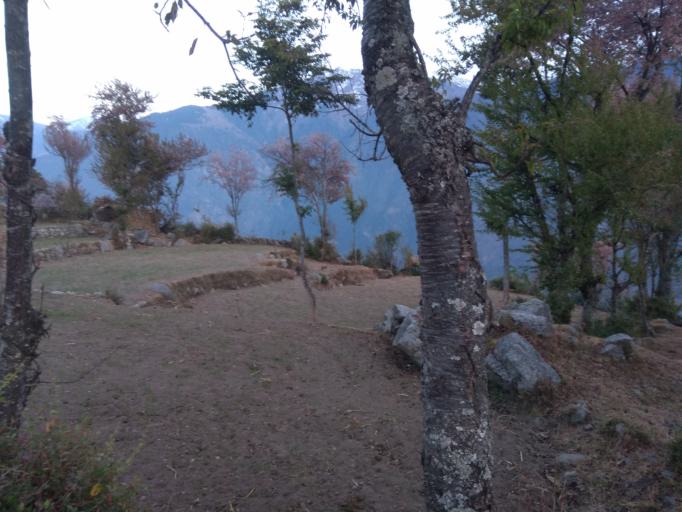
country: NP
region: Far Western
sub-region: Seti Zone
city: Achham
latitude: 29.2413
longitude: 81.6404
